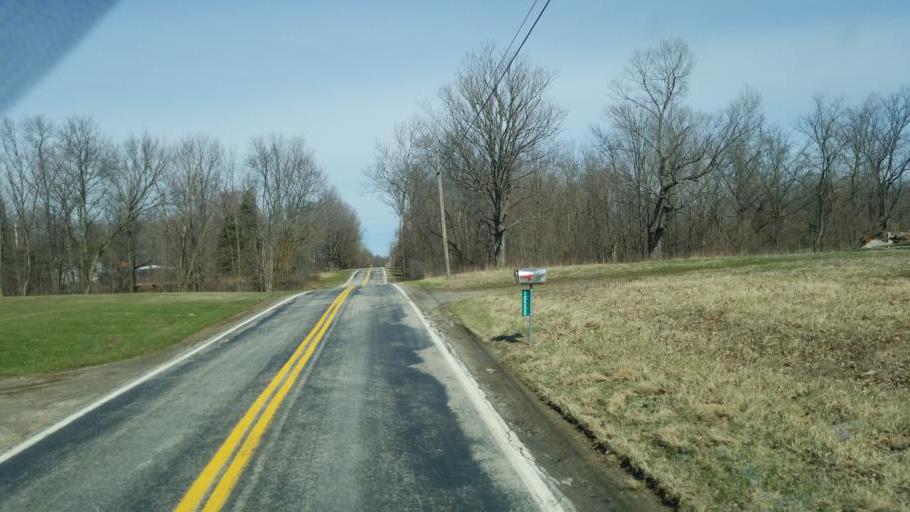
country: US
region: Ohio
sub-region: Lorain County
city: South Amherst
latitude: 41.3381
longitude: -82.2883
